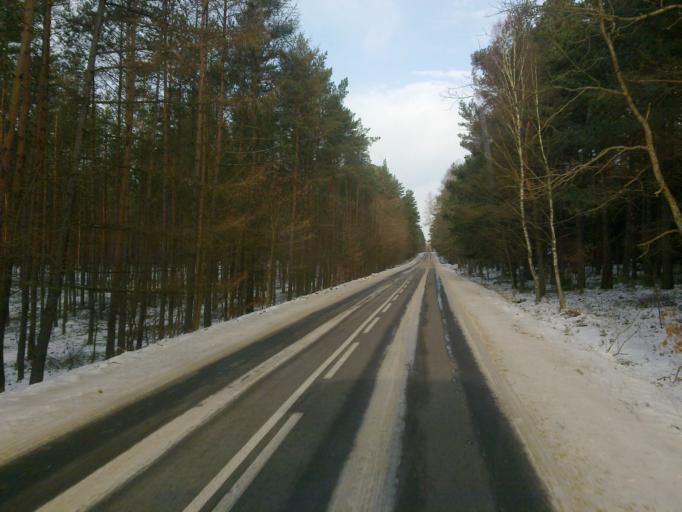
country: PL
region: Pomeranian Voivodeship
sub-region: Powiat wejherowski
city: Orle
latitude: 54.6948
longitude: 18.1826
